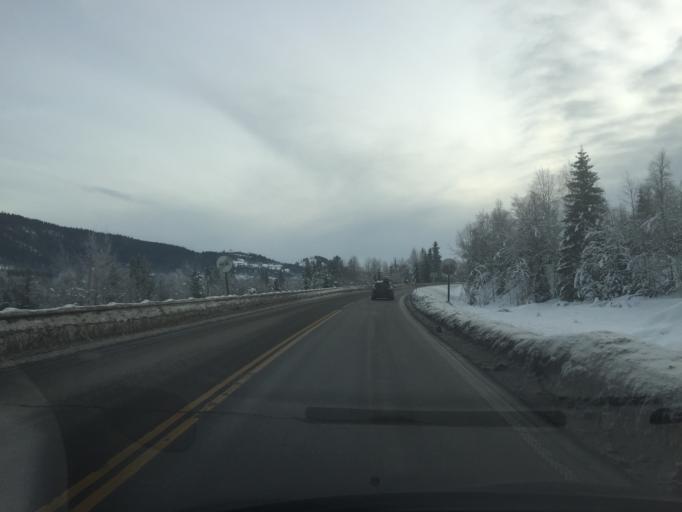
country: NO
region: Hedmark
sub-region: Trysil
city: Innbygda
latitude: 61.2702
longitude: 12.3015
